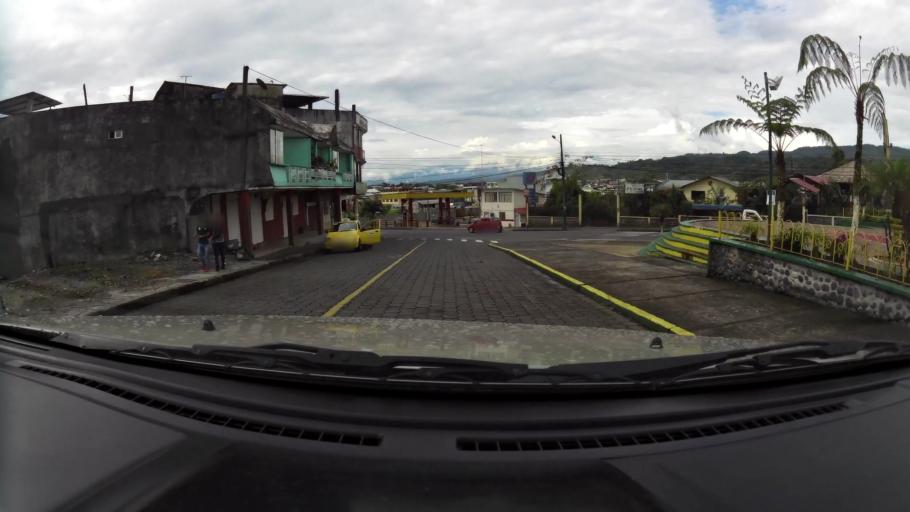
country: EC
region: Pastaza
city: Puyo
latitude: -1.4781
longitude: -77.9998
